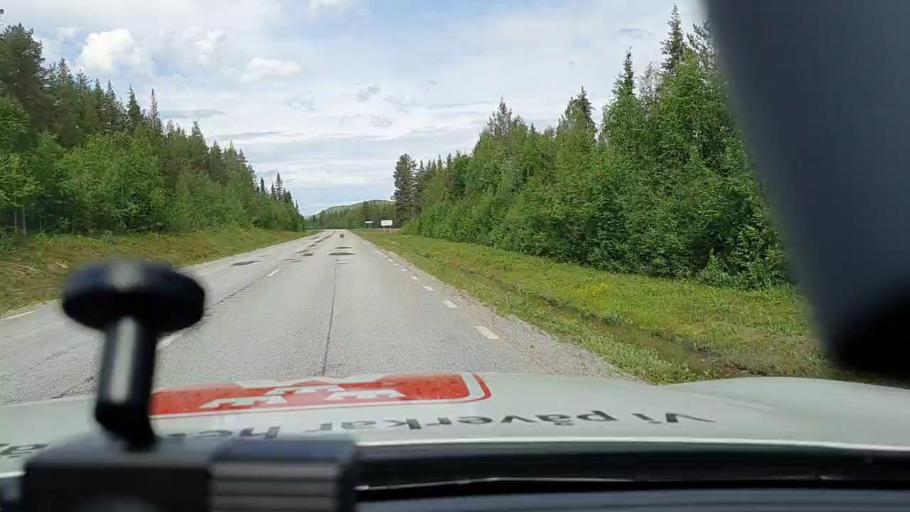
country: SE
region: Norrbotten
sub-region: Jokkmokks Kommun
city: Jokkmokk
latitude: 66.5516
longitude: 20.1185
